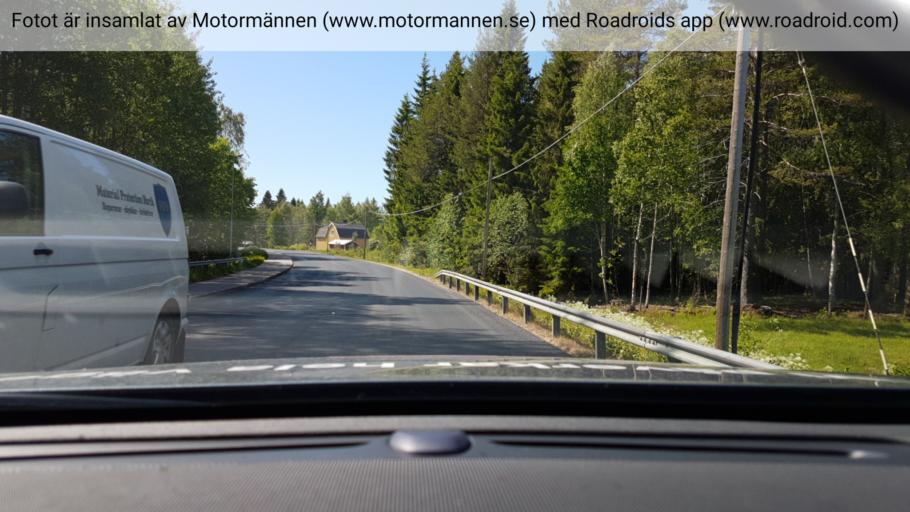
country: SE
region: Vaesterbotten
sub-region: Nordmalings Kommun
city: Nordmaling
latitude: 63.5781
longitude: 19.5282
